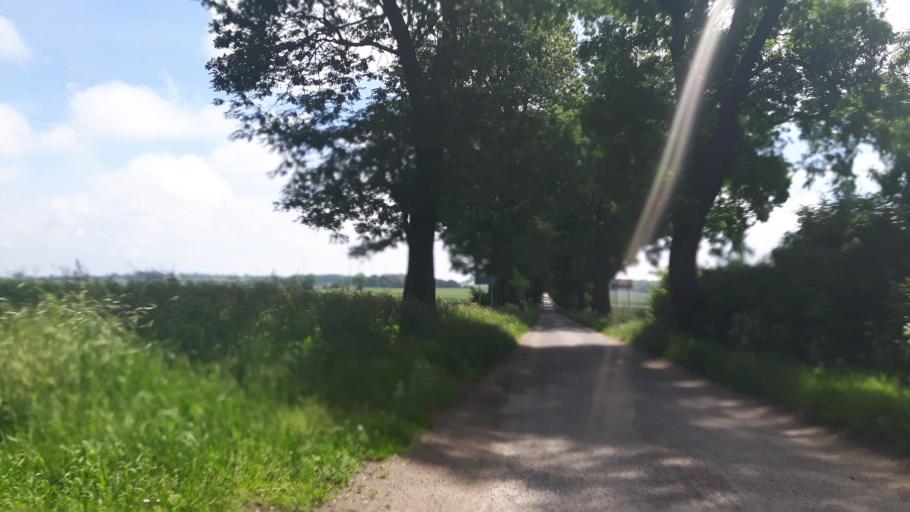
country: PL
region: West Pomeranian Voivodeship
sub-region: Powiat slawienski
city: Darlowo
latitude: 54.4709
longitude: 16.4723
